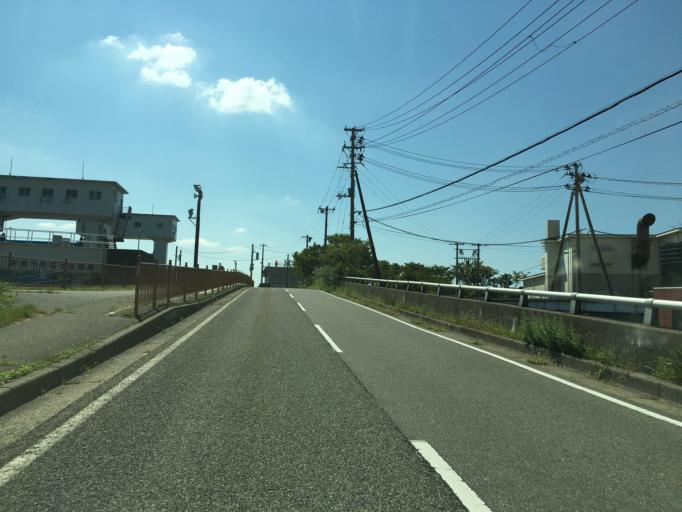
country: JP
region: Niigata
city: Niigata-shi
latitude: 37.8981
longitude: 139.0128
